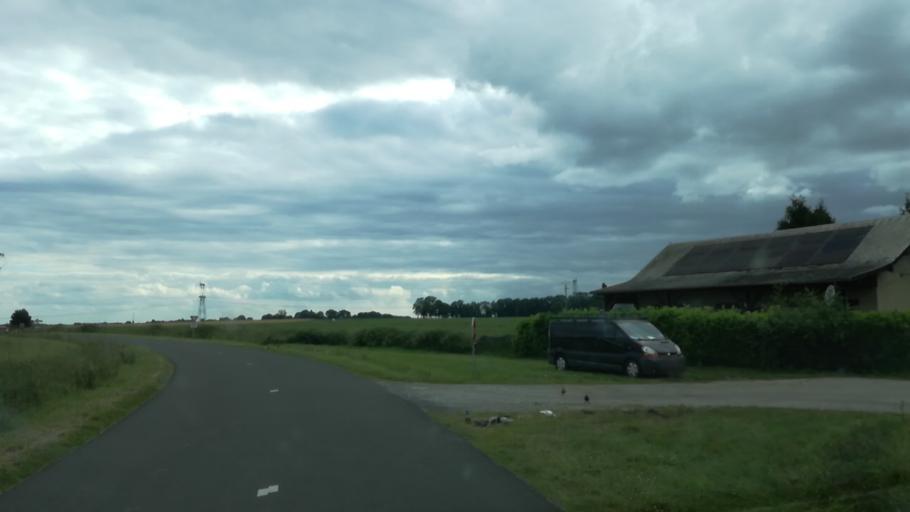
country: FR
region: Haute-Normandie
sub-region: Departement de l'Eure
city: Bourg-Achard
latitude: 49.3042
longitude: 0.7947
